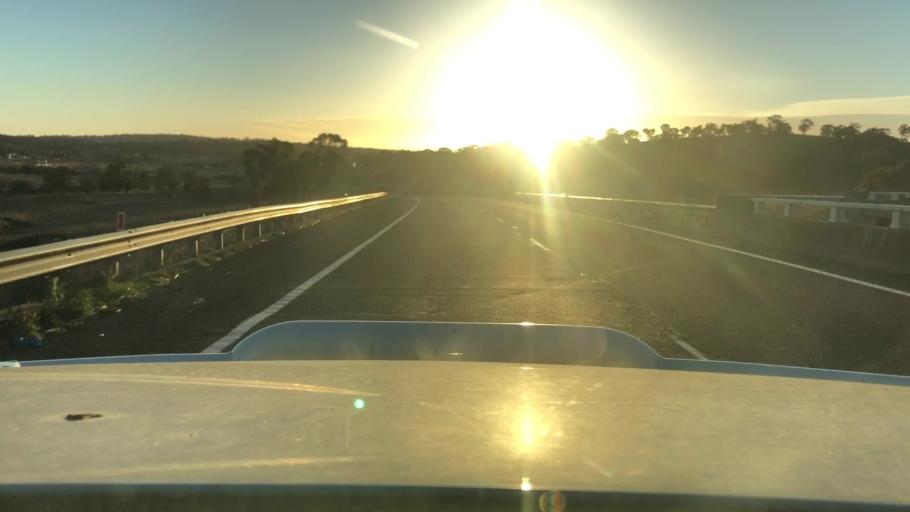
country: AU
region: New South Wales
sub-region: Goulburn Mulwaree
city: Goulburn
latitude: -34.7866
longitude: 149.6567
